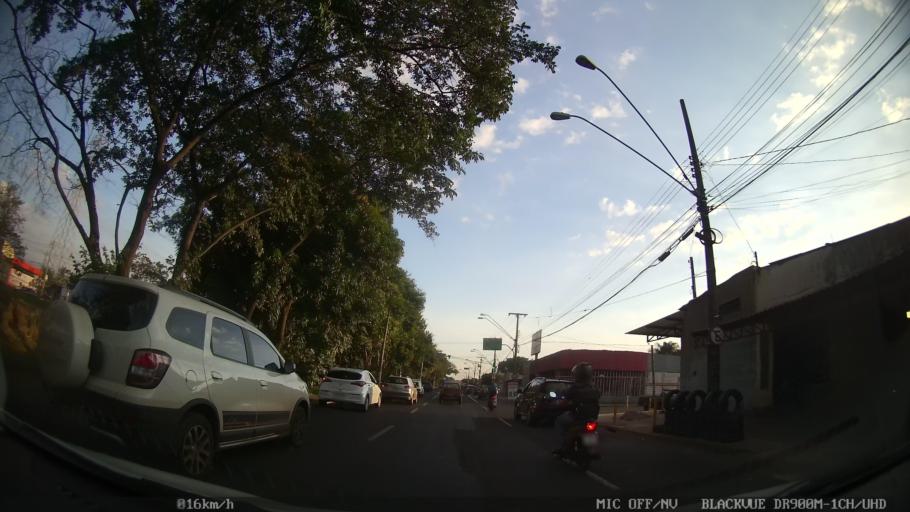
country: BR
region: Sao Paulo
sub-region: Ribeirao Preto
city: Ribeirao Preto
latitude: -21.1466
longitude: -47.8058
